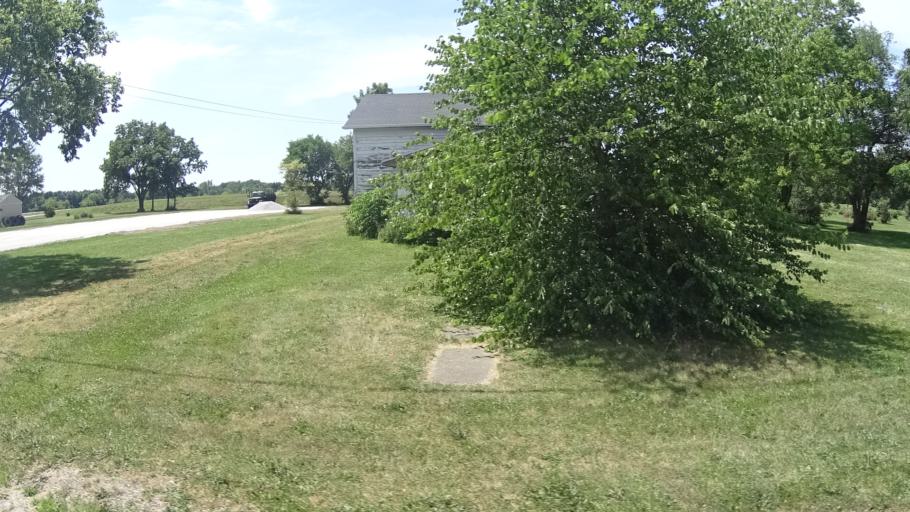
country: US
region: Ohio
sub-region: Erie County
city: Sandusky
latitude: 41.4416
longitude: -82.7727
